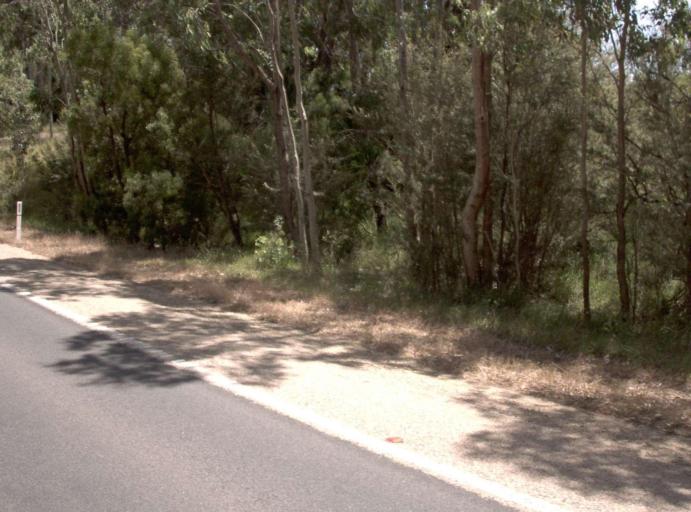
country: AU
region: Victoria
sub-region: East Gippsland
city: Bairnsdale
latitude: -37.7566
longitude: 147.7109
